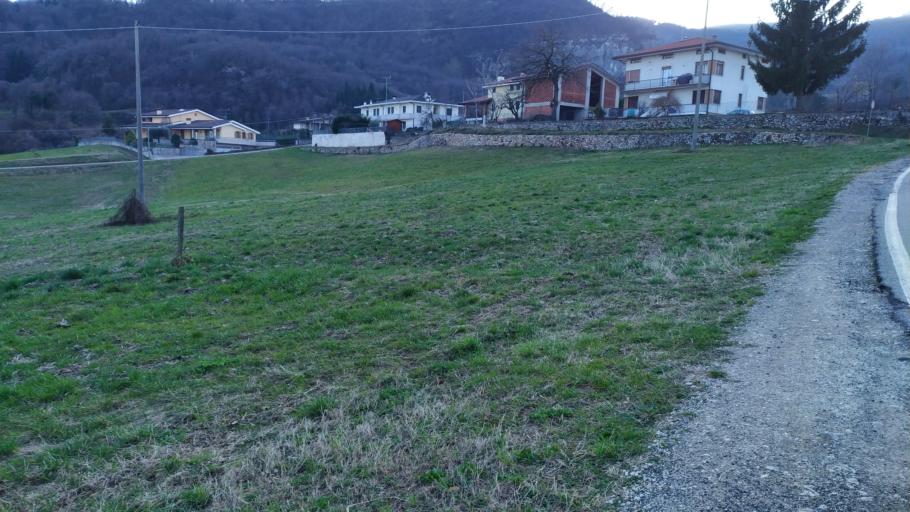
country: IT
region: Veneto
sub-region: Provincia di Vicenza
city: Monte di Malo
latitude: 45.6615
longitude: 11.3540
